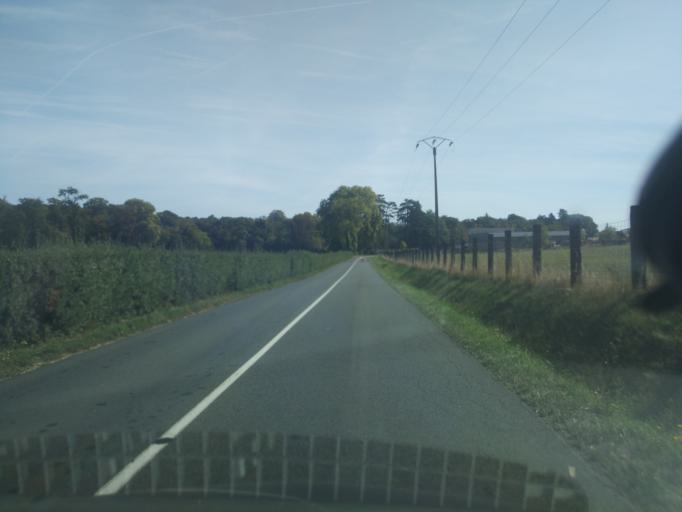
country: FR
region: Ile-de-France
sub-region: Departement de l'Essonne
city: Forges-les-Bains
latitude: 48.6410
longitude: 2.0956
